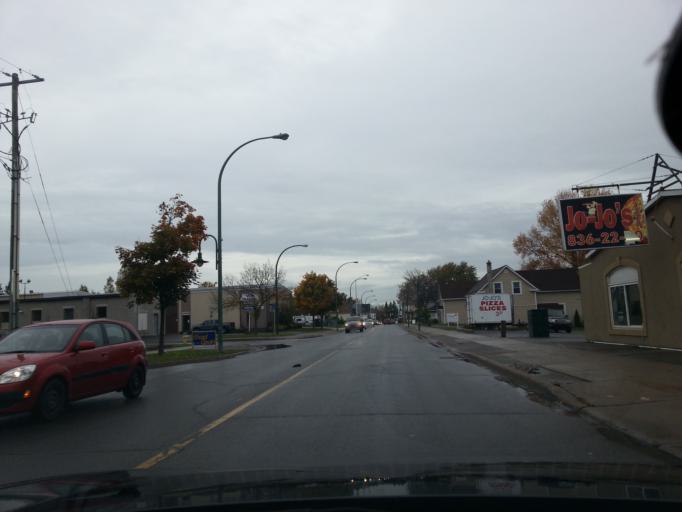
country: CA
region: Ontario
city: Bells Corners
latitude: 45.2561
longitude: -75.9181
